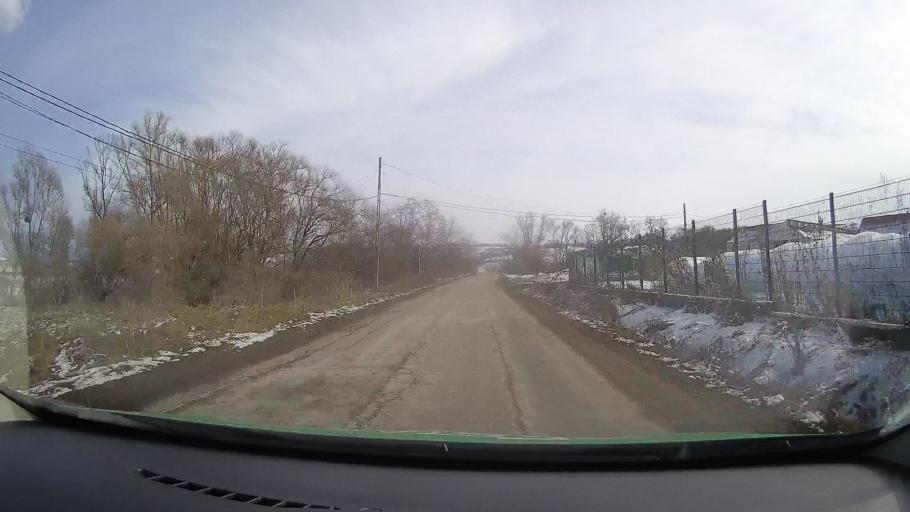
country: RO
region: Mures
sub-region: Comuna Apold
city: Apold
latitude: 46.1201
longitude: 24.8233
